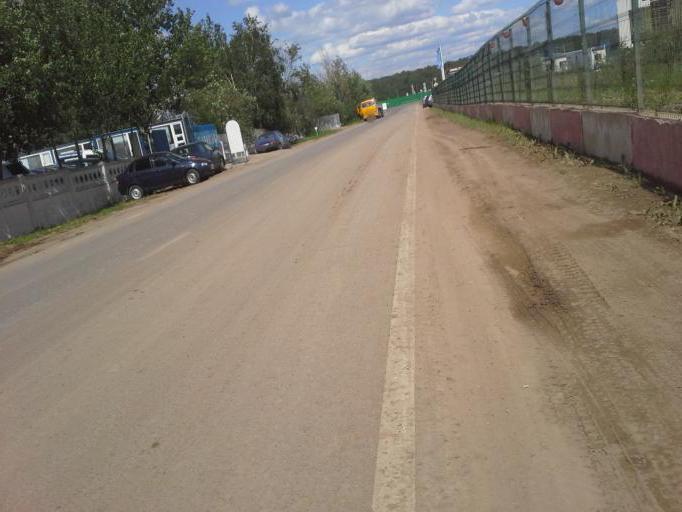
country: RU
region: Moskovskaya
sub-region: Leninskiy Rayon
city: Vnukovo
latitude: 55.6207
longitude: 37.2644
